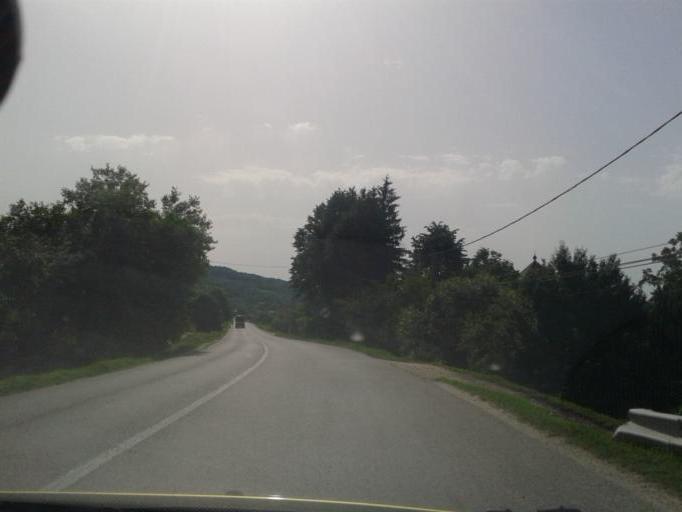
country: RO
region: Valcea
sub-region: Comuna Bunesti
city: Bunesti
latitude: 45.1087
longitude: 24.1889
